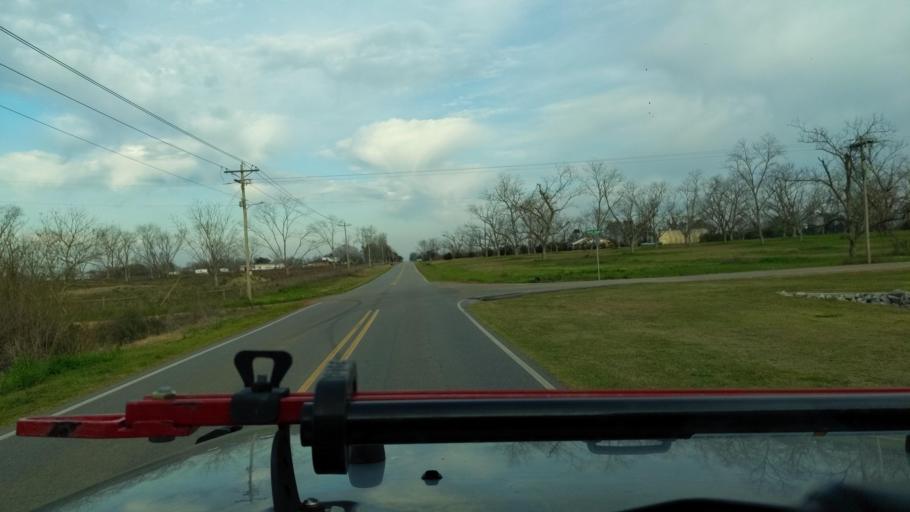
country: US
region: Alabama
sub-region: Baldwin County
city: Foley
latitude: 30.4580
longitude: -87.7260
